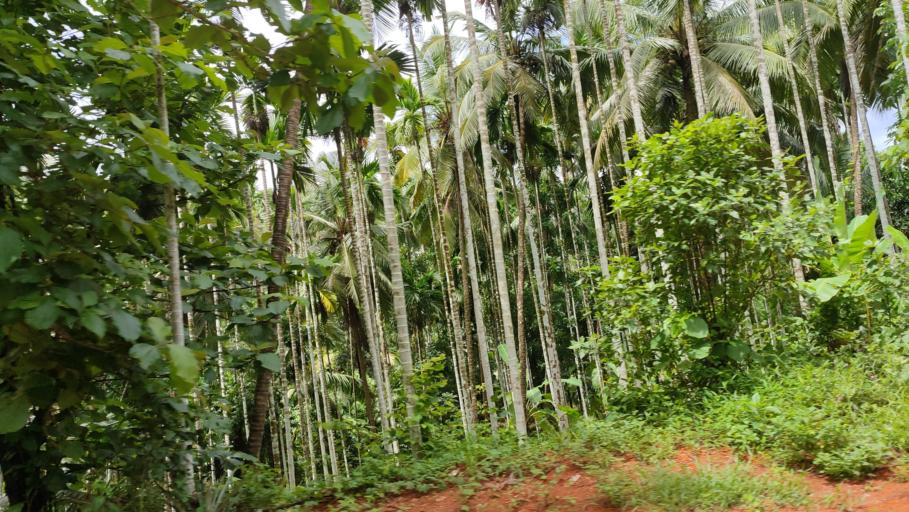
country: IN
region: Kerala
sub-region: Kasaragod District
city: Nileshwar
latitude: 12.2954
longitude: 75.2757
